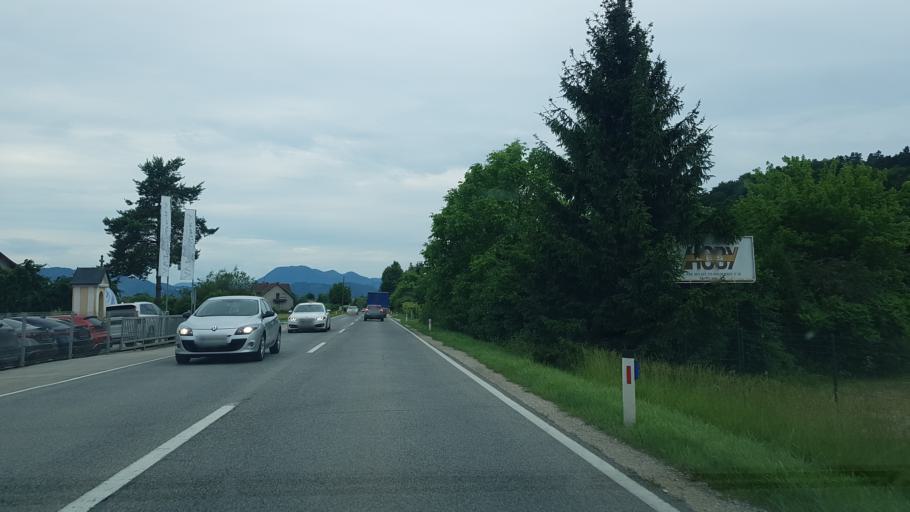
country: SI
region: Celje
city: Trnovlje pri Celju
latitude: 46.2739
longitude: 15.2955
